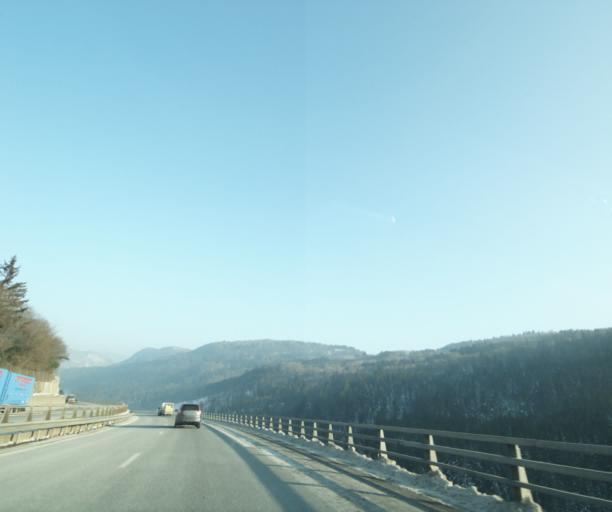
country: FR
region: Rhone-Alpes
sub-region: Departement de l'Ain
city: Nantua
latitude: 46.1646
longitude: 5.6996
